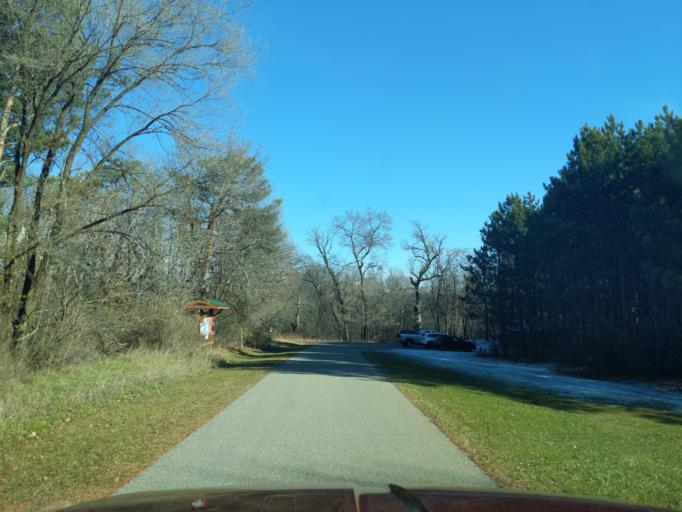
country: US
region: Wisconsin
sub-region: Waushara County
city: Silver Lake
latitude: 44.1209
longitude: -89.1745
